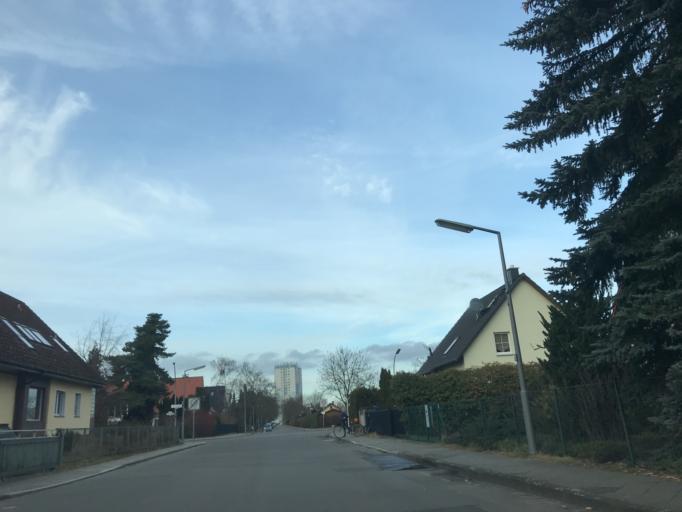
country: DE
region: Berlin
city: Wilhelmstadt
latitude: 52.5253
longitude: 13.1663
